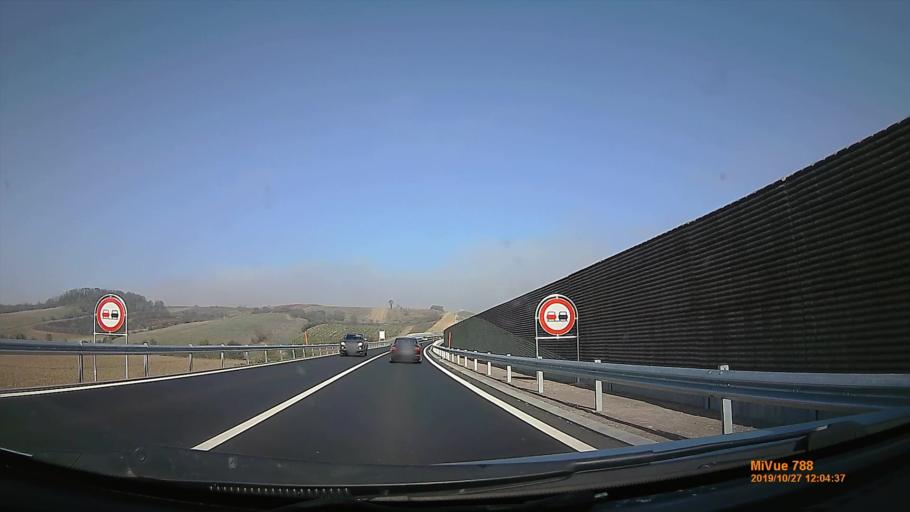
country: AT
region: Lower Austria
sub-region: Politischer Bezirk Mistelbach
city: Drasenhofen
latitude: 48.7551
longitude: 16.6344
